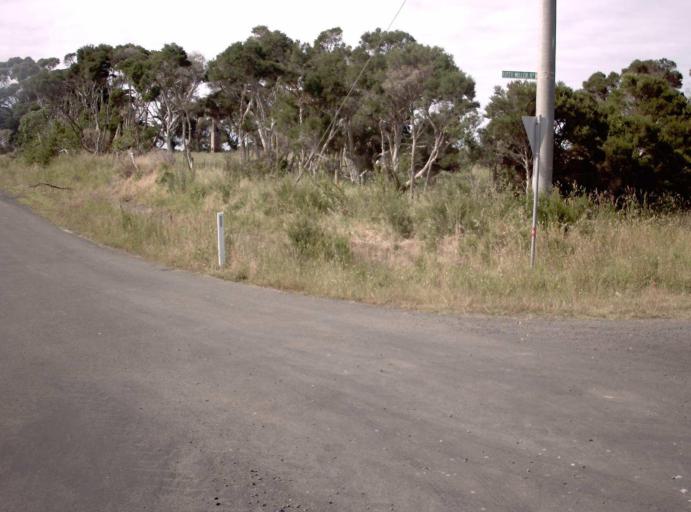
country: AU
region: Victoria
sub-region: Bass Coast
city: Phillip Island
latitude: -38.4876
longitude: 145.1700
